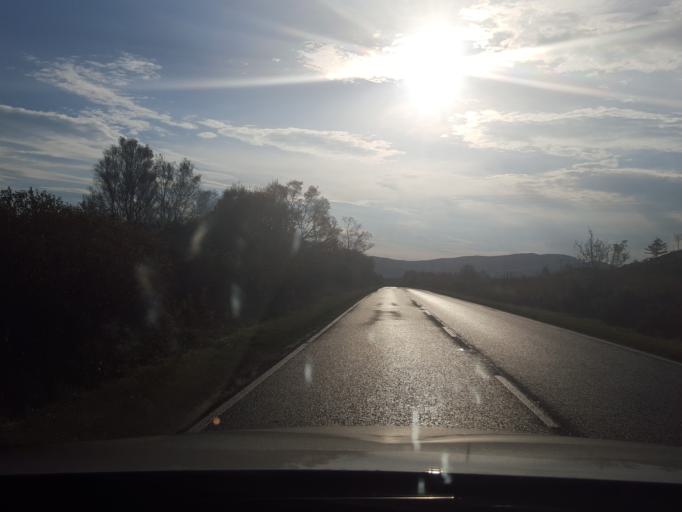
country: GB
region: Scotland
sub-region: Highland
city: Portree
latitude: 57.2559
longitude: -5.9394
